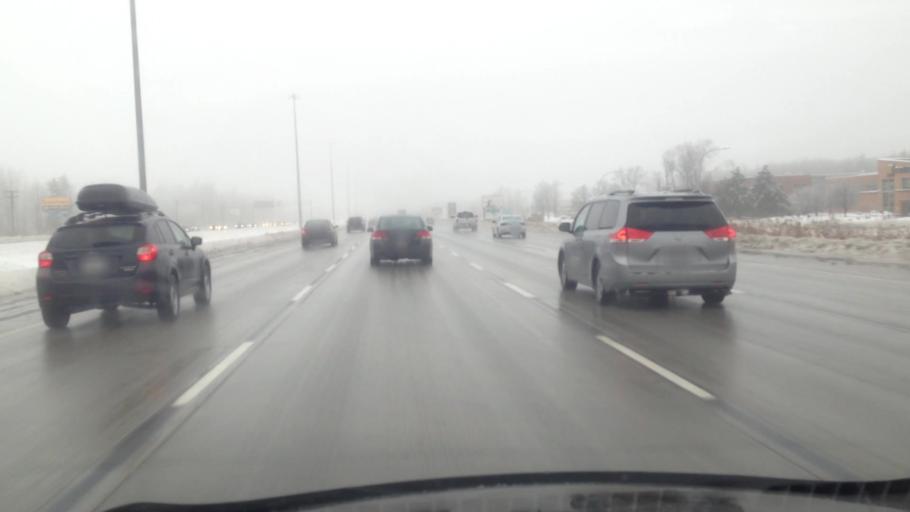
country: CA
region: Quebec
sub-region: Laurentides
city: Blainville
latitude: 45.6669
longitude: -73.8987
